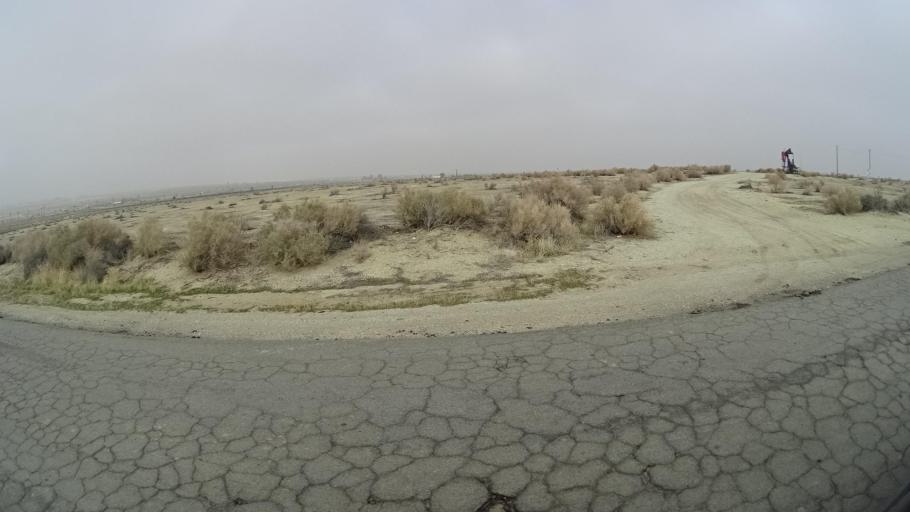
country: US
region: California
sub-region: Kern County
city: Maricopa
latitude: 35.0382
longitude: -119.3720
